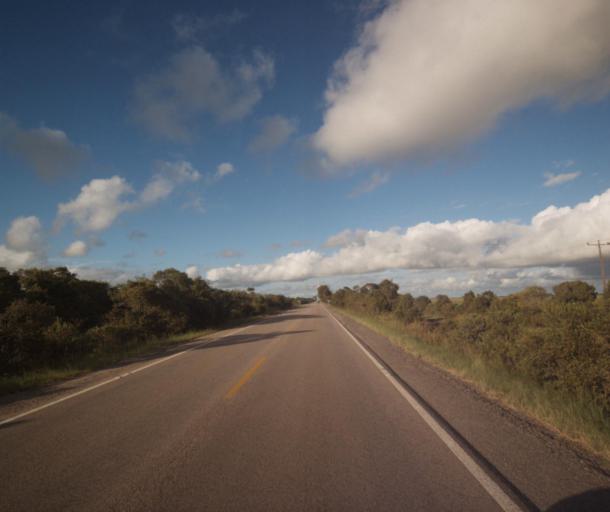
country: BR
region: Rio Grande do Sul
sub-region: Rio Grande
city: Rio Grande
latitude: -32.1823
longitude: -52.4247
